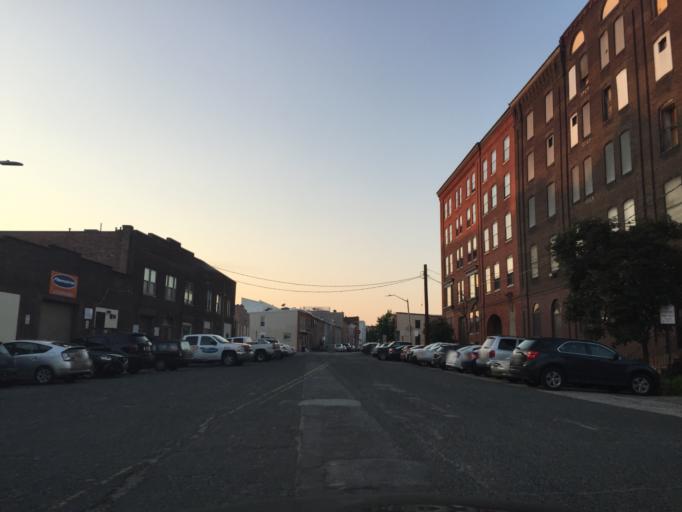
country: US
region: Maryland
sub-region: City of Baltimore
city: Baltimore
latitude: 39.2676
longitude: -76.6120
